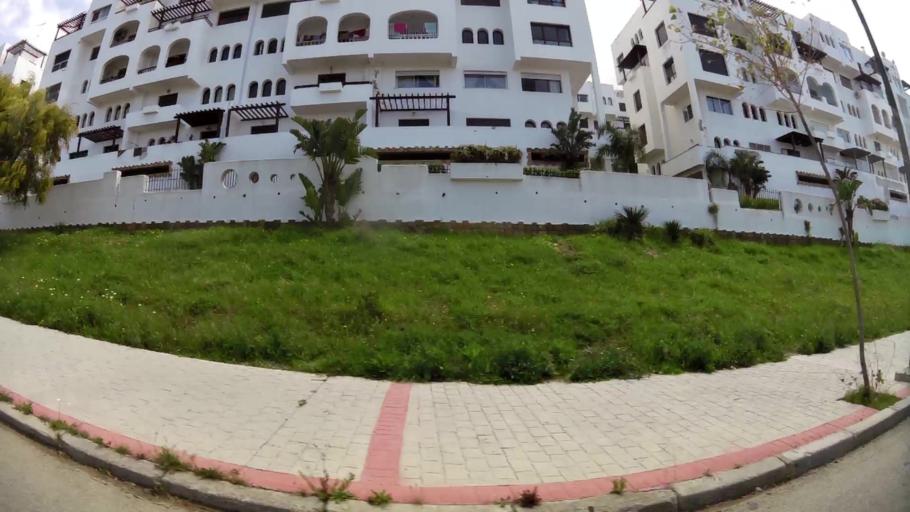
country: MA
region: Tanger-Tetouan
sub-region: Tanger-Assilah
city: Tangier
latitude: 35.7808
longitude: -5.7607
